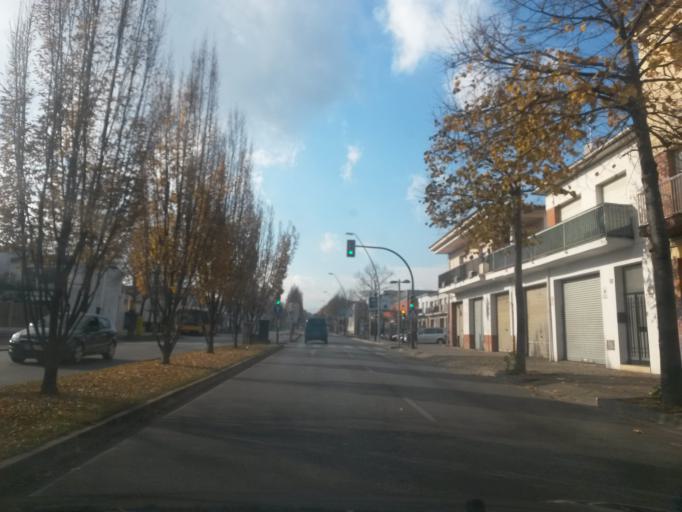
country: ES
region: Catalonia
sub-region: Provincia de Girona
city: Salt
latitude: 41.9722
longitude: 2.7890
